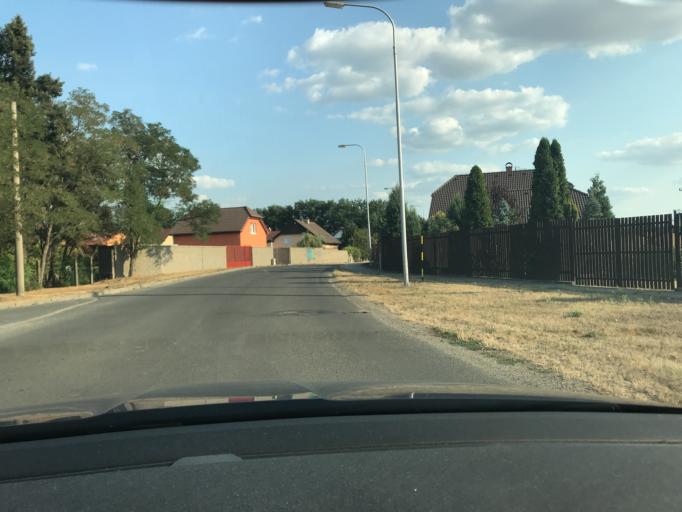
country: CZ
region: Ustecky
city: Postoloprty
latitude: 50.3640
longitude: 13.6909
